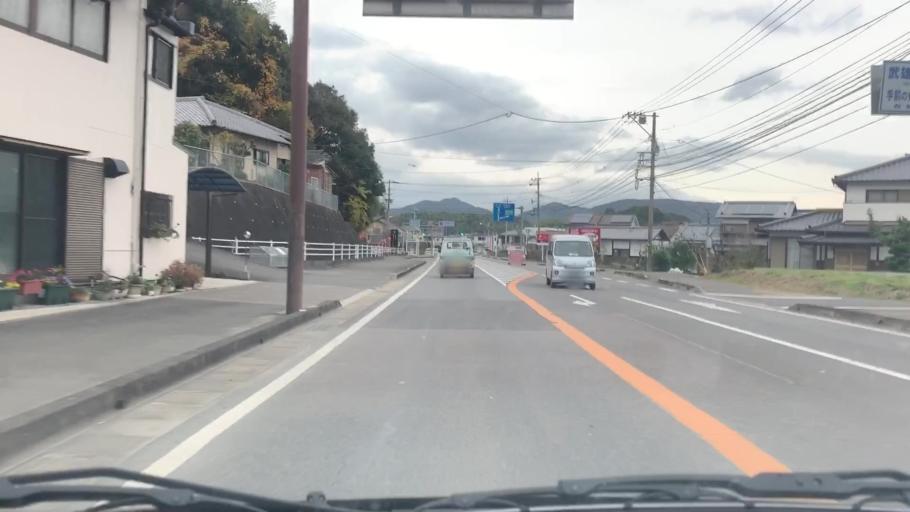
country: JP
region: Saga Prefecture
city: Takeocho-takeo
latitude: 33.1844
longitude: 130.0390
